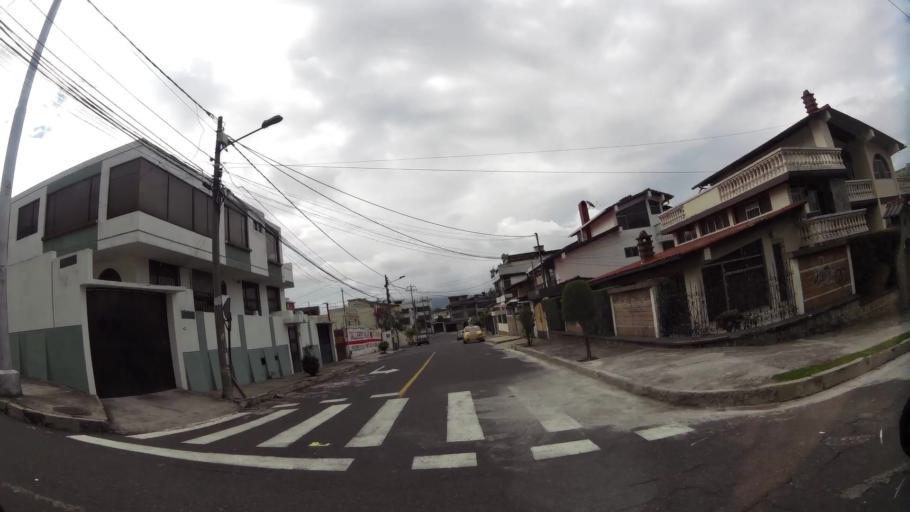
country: EC
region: Pichincha
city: Quito
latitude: -0.1421
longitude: -78.4981
